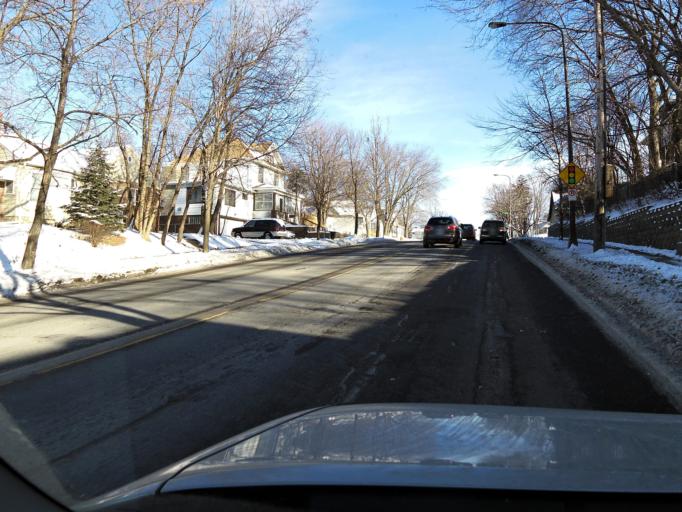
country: US
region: Minnesota
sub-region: Ramsey County
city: Saint Paul
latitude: 44.9774
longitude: -93.0782
